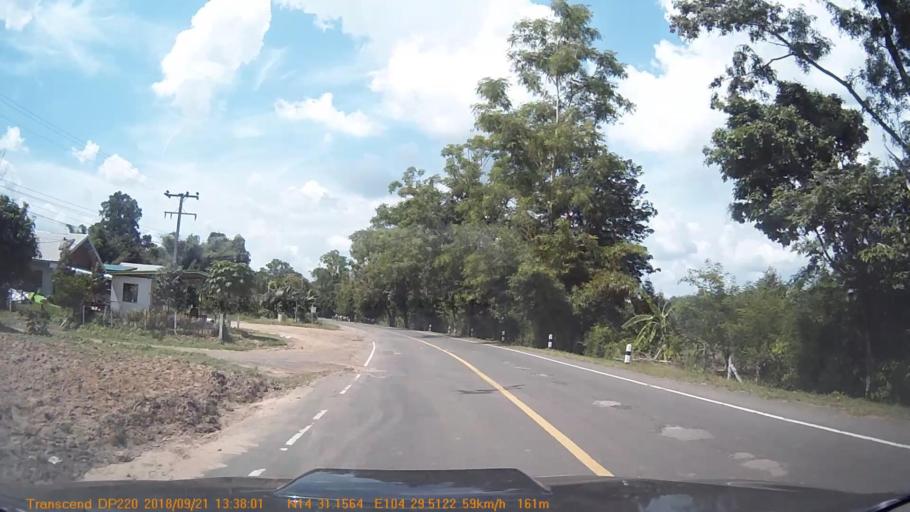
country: TH
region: Sisaket
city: Khun Han
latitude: 14.5194
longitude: 104.4919
